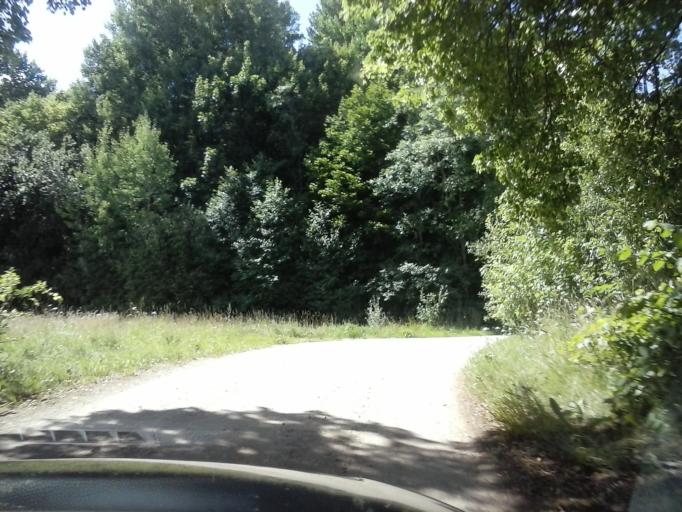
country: LV
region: Apes Novads
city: Ape
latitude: 57.5707
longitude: 26.6701
